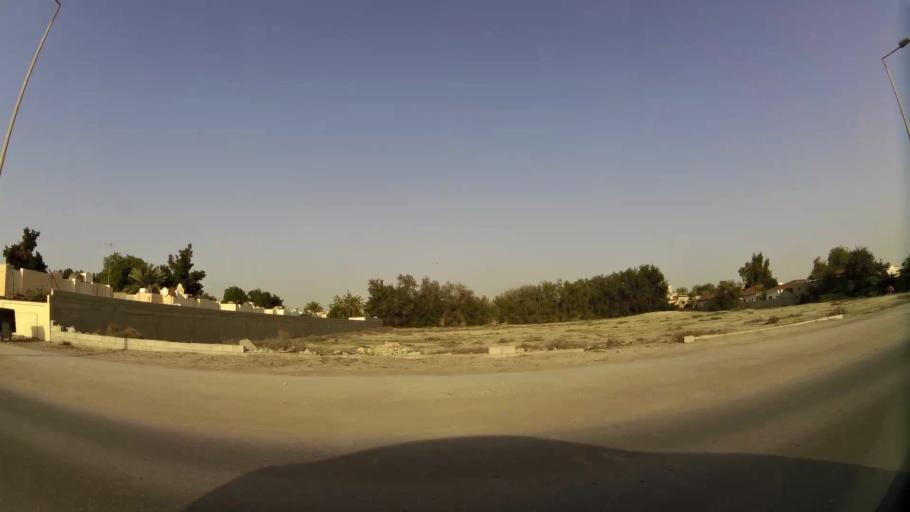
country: BH
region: Manama
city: Jidd Hafs
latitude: 26.1991
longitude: 50.4853
